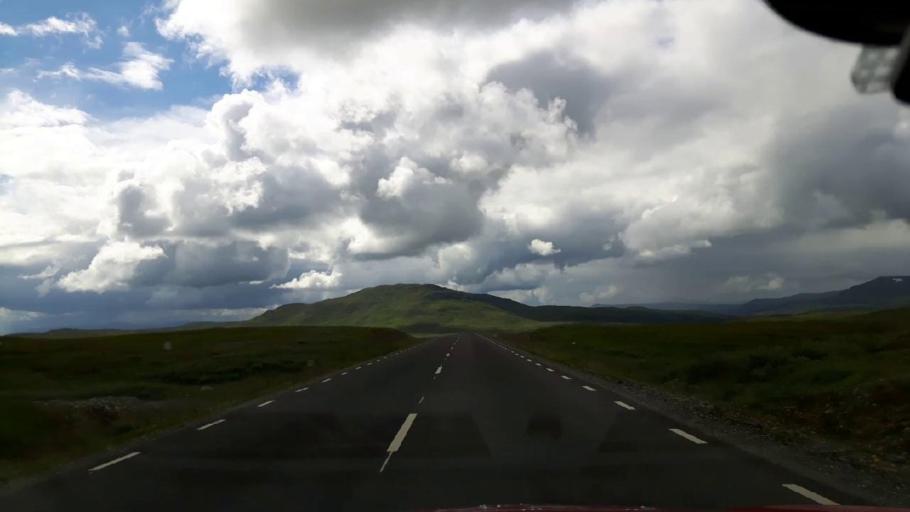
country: NO
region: Nordland
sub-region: Hattfjelldal
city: Hattfjelldal
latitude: 65.0412
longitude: 14.3284
